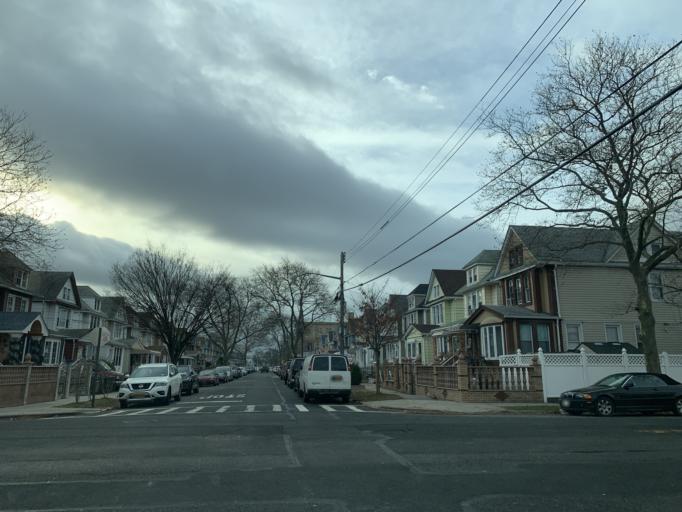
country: US
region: New York
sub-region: Queens County
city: Jamaica
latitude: 40.6817
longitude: -73.8108
